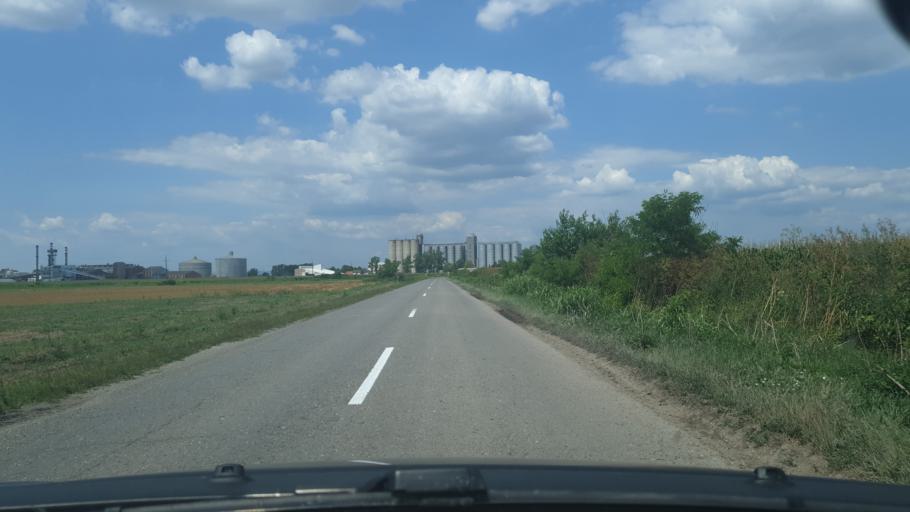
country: RS
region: Autonomna Pokrajina Vojvodina
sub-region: Sremski Okrug
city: Pecinci
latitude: 44.8787
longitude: 19.9610
